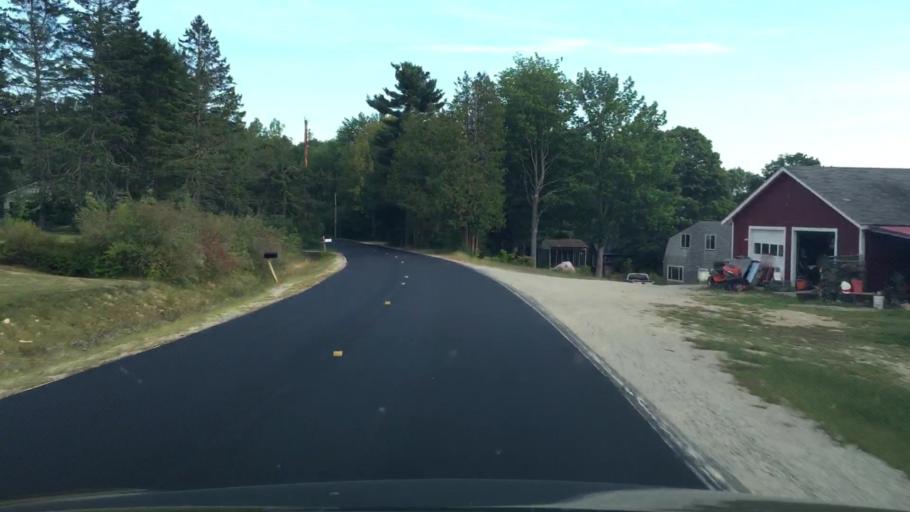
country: US
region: Maine
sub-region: Hancock County
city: Orland
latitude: 44.5458
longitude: -68.6199
